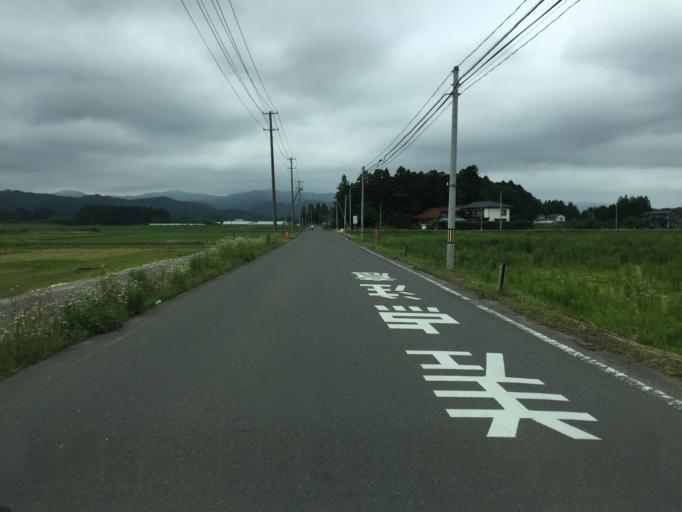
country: JP
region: Fukushima
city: Namie
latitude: 37.7223
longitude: 140.9430
